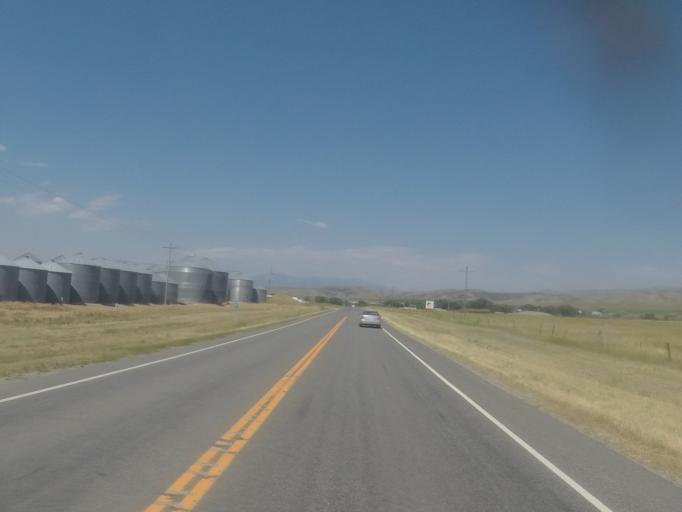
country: US
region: Montana
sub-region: Broadwater County
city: Townsend
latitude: 46.1645
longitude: -111.4537
